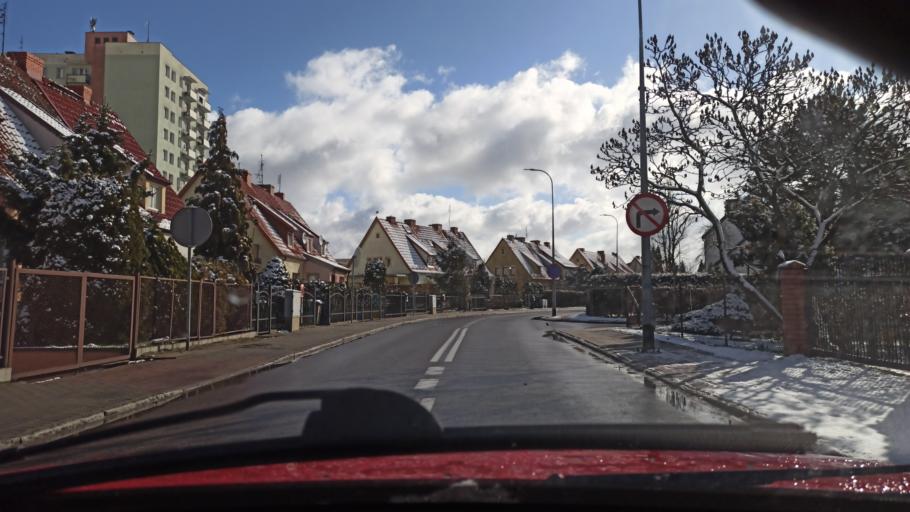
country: PL
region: Warmian-Masurian Voivodeship
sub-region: Powiat elblaski
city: Elblag
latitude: 54.1457
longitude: 19.4044
